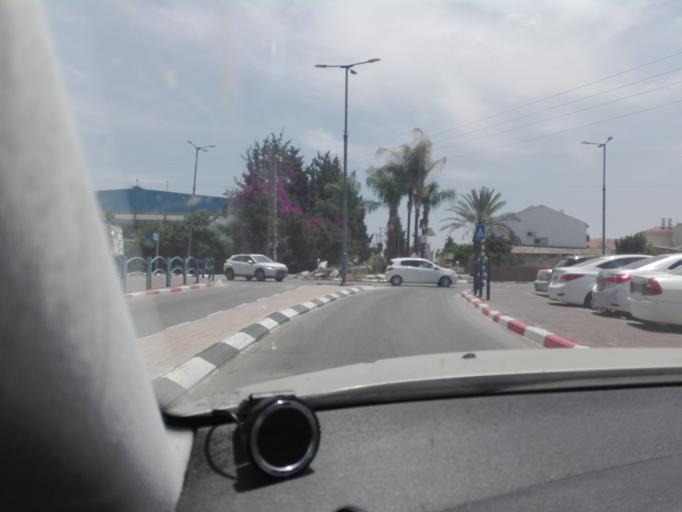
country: IL
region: Central District
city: Bene 'Ayish
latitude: 31.7363
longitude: 34.7513
